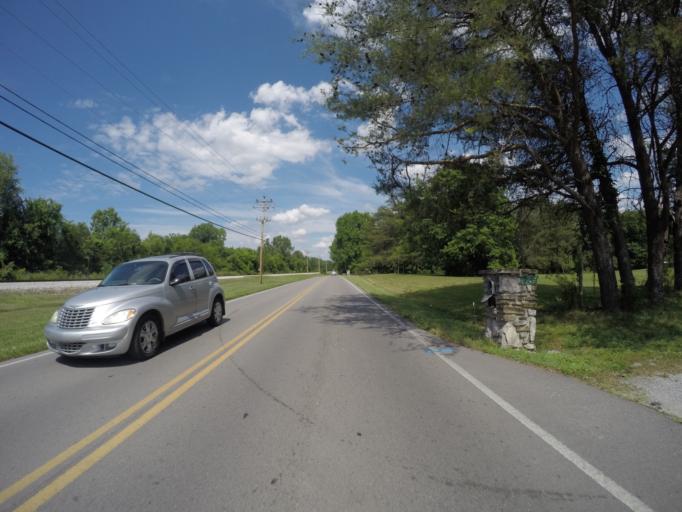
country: US
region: Tennessee
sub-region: Wilson County
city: Green Hill
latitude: 36.2049
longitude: -86.5477
